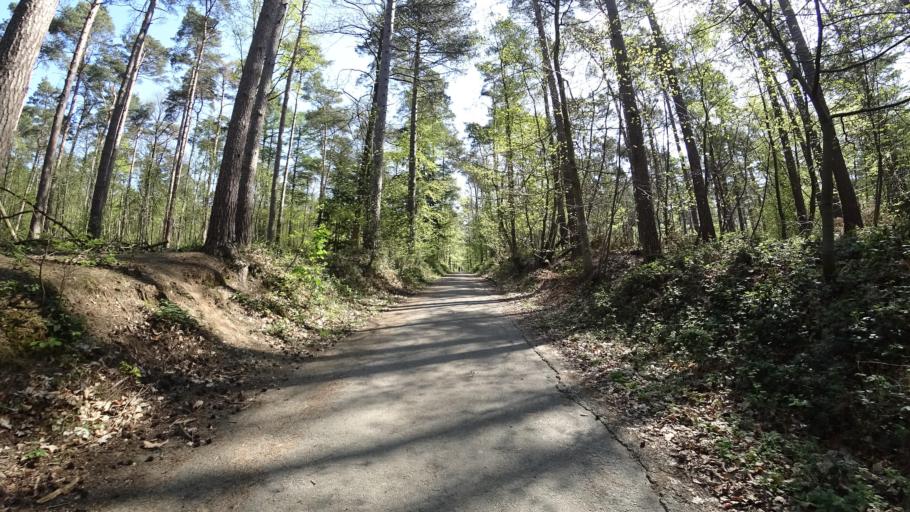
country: BE
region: Wallonia
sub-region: Province du Brabant Wallon
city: Braine-le-Chateau
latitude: 50.7042
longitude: 4.2999
